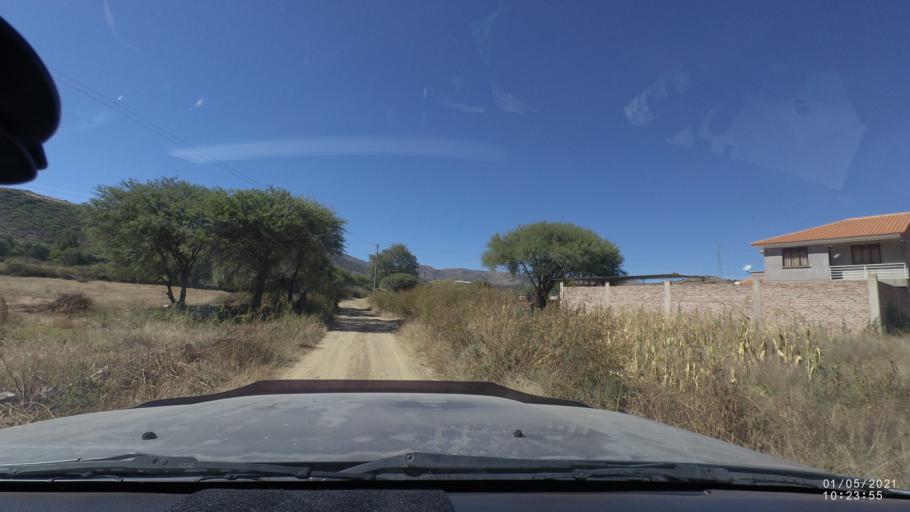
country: BO
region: Cochabamba
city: Capinota
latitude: -17.5735
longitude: -66.1958
